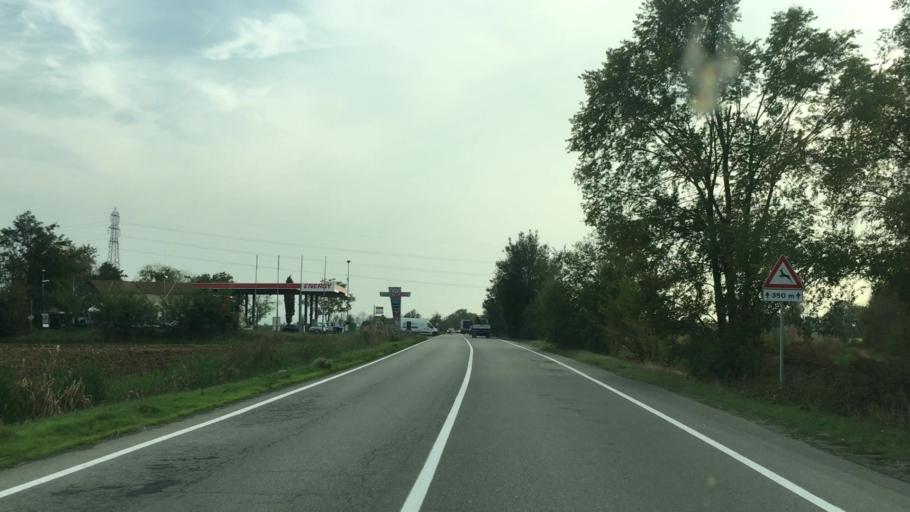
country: IT
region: Emilia-Romagna
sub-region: Provincia di Reggio Emilia
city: Calerno
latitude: 44.7574
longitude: 10.4967
